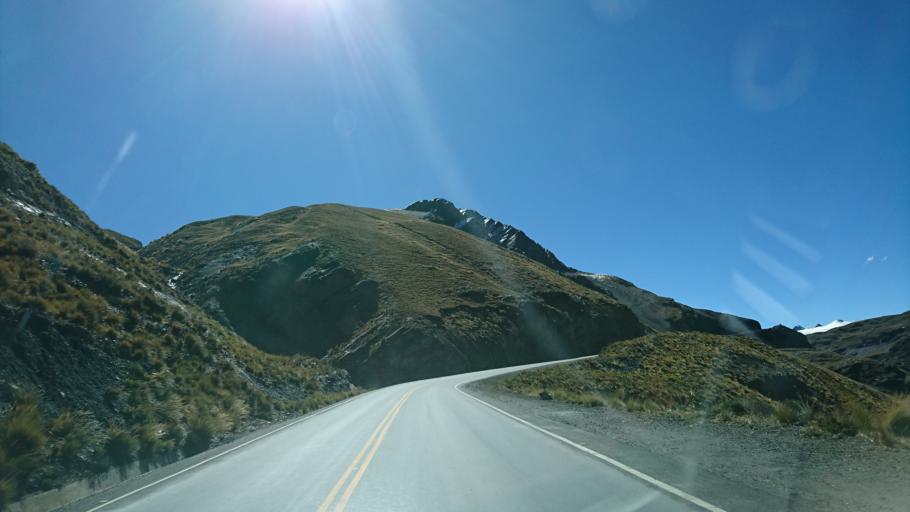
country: BO
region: La Paz
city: La Paz
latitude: -16.3942
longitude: -68.0443
